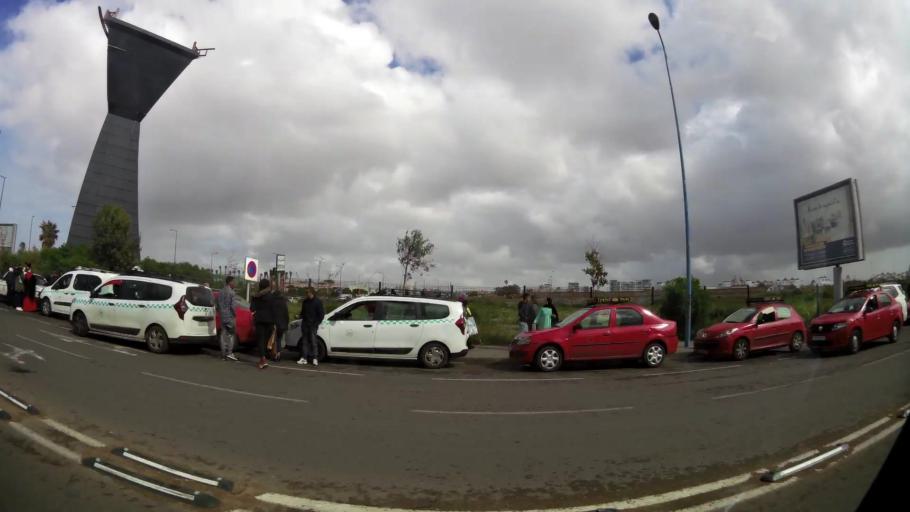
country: MA
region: Grand Casablanca
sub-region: Casablanca
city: Casablanca
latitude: 33.5772
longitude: -7.7047
